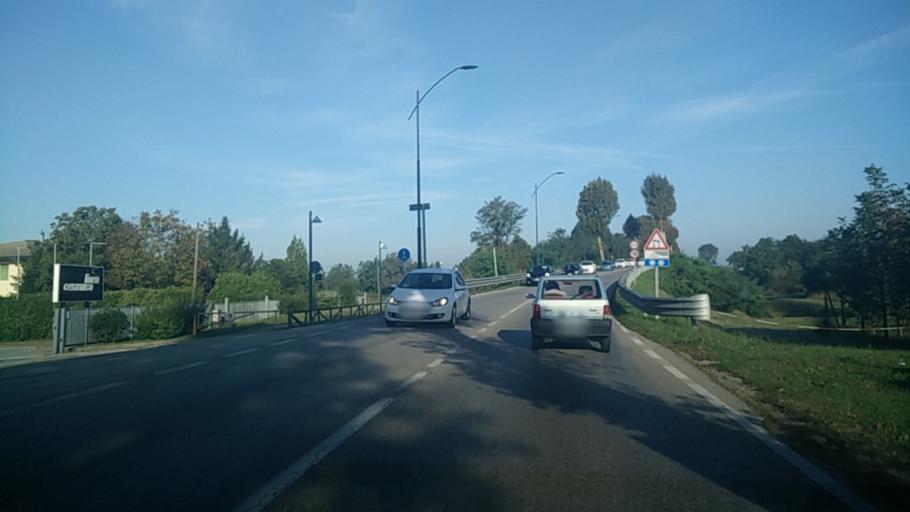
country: IT
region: Veneto
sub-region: Provincia di Venezia
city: Zelarino
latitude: 45.5182
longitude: 12.2016
